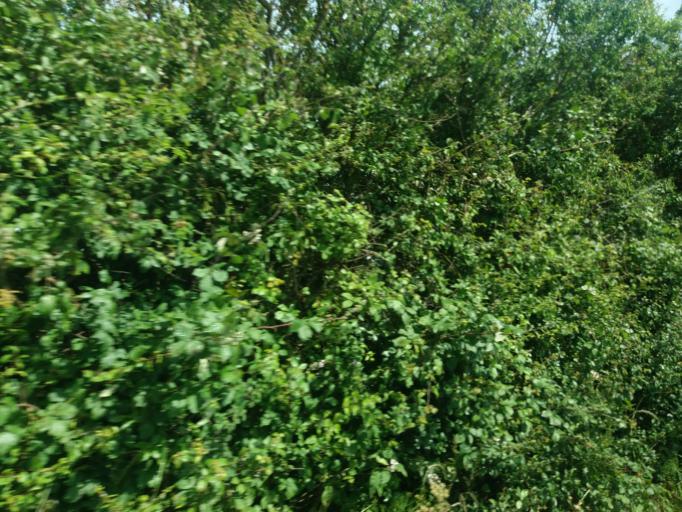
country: IE
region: Leinster
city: Lusk
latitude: 53.5384
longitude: -6.1896
